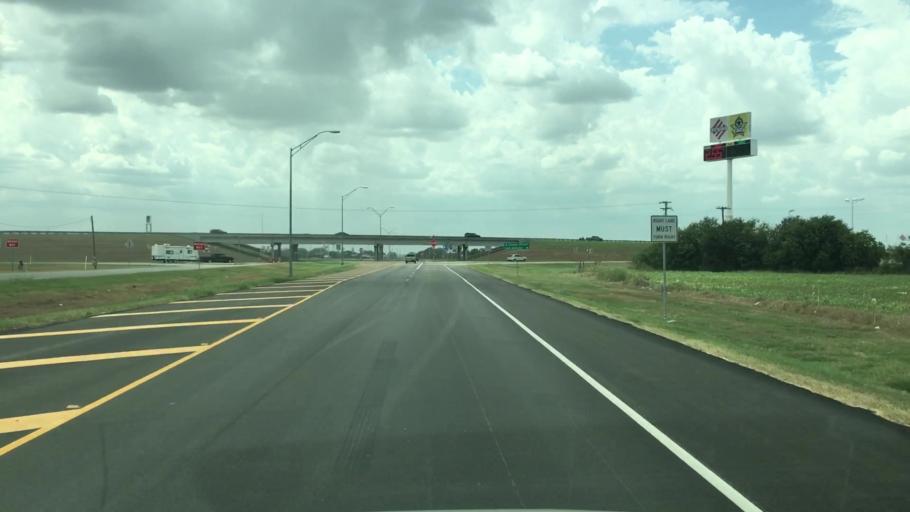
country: US
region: Texas
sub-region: Live Oak County
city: George West
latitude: 28.3381
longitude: -98.0239
